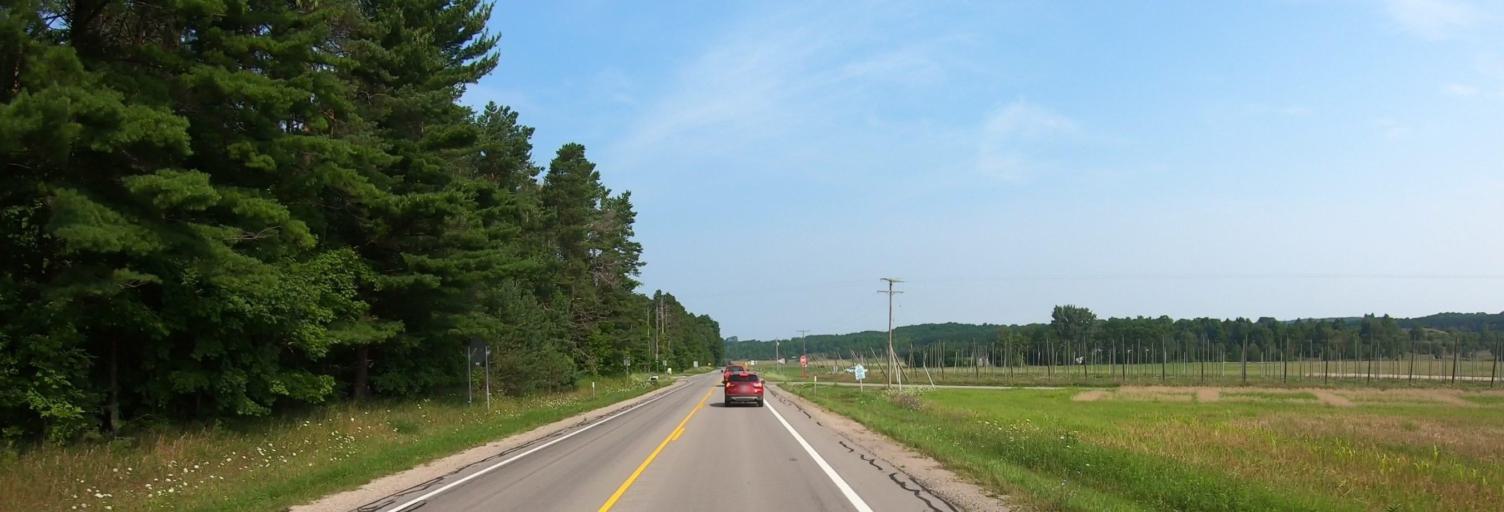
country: US
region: Michigan
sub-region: Benzie County
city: Beulah
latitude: 44.8074
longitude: -86.0182
